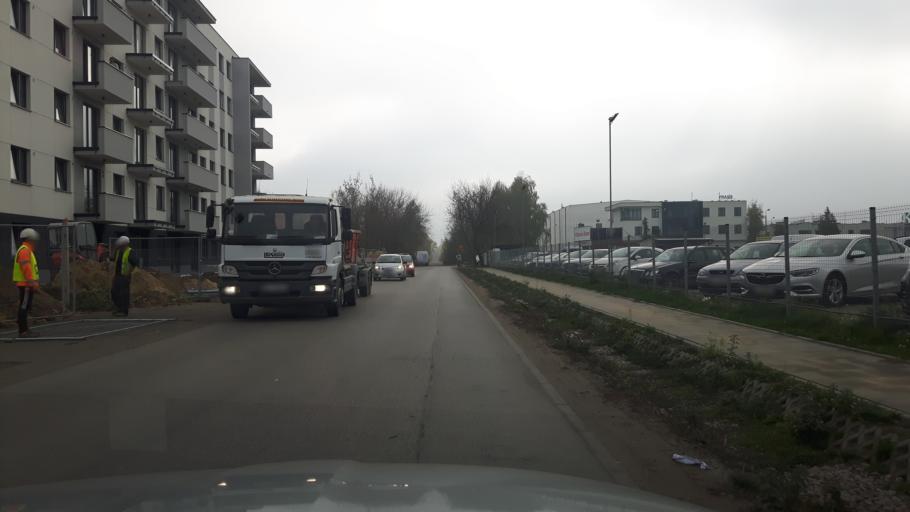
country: PL
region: Masovian Voivodeship
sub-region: Warszawa
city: Wlochy
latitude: 52.2014
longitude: 20.9447
